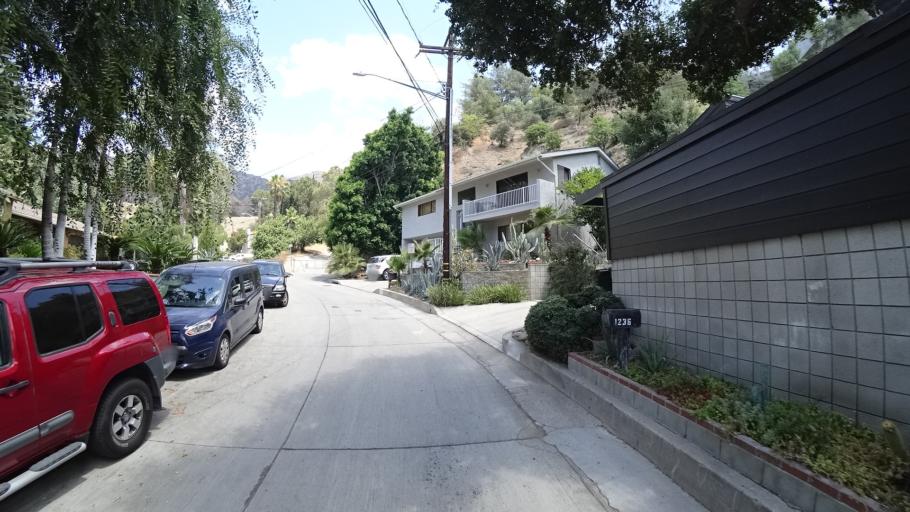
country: US
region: California
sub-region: Los Angeles County
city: Burbank
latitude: 34.1892
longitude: -118.2860
